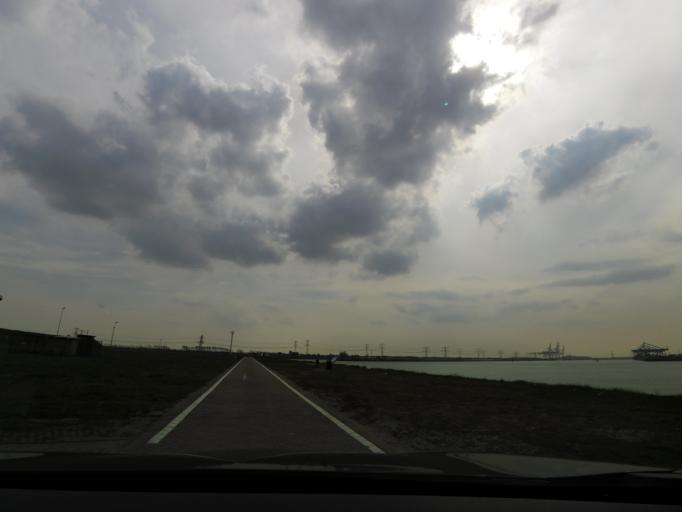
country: NL
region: South Holland
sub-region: Gemeente Rotterdam
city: Hoek van Holland
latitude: 51.9445
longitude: 4.0840
